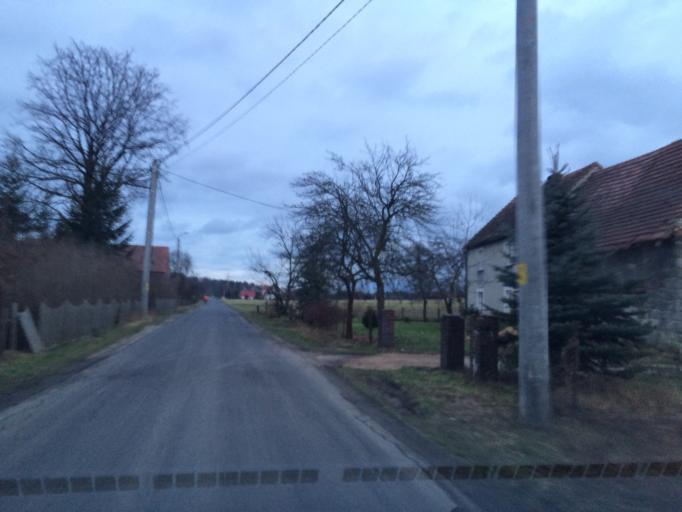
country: PL
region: Lower Silesian Voivodeship
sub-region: Powiat boleslawiecki
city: Nowogrodziec
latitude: 51.1980
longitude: 15.4443
